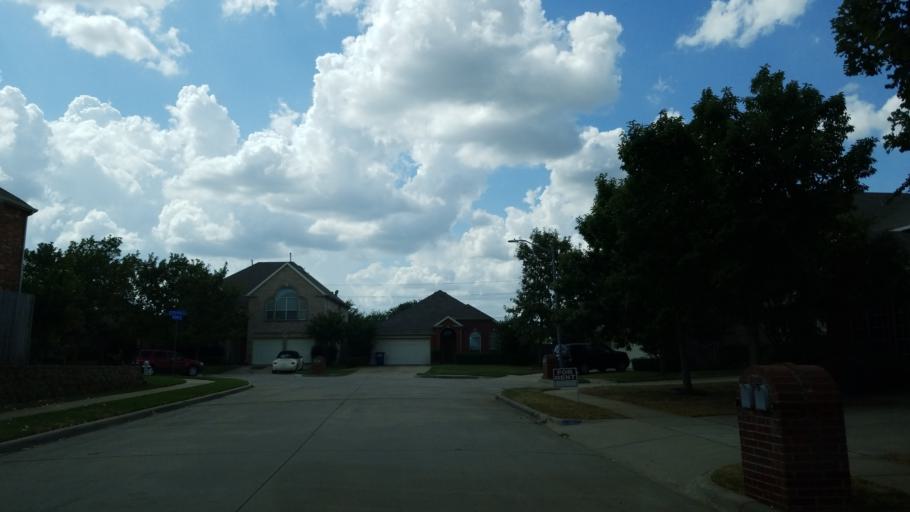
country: US
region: Texas
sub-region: Tarrant County
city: Euless
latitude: 32.8806
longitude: -97.0813
